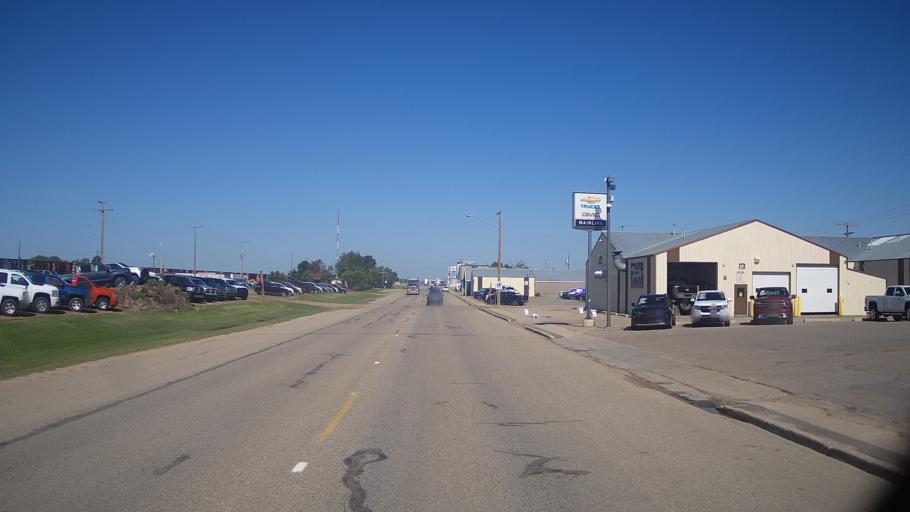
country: CA
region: Saskatchewan
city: Watrous
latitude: 51.6708
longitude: -105.4656
